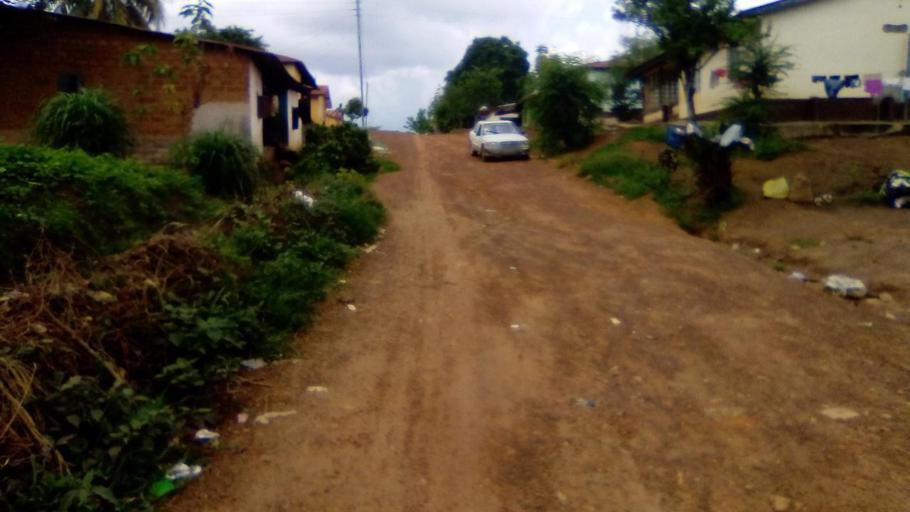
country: SL
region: Southern Province
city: Bo
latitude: 7.9607
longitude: -11.7247
